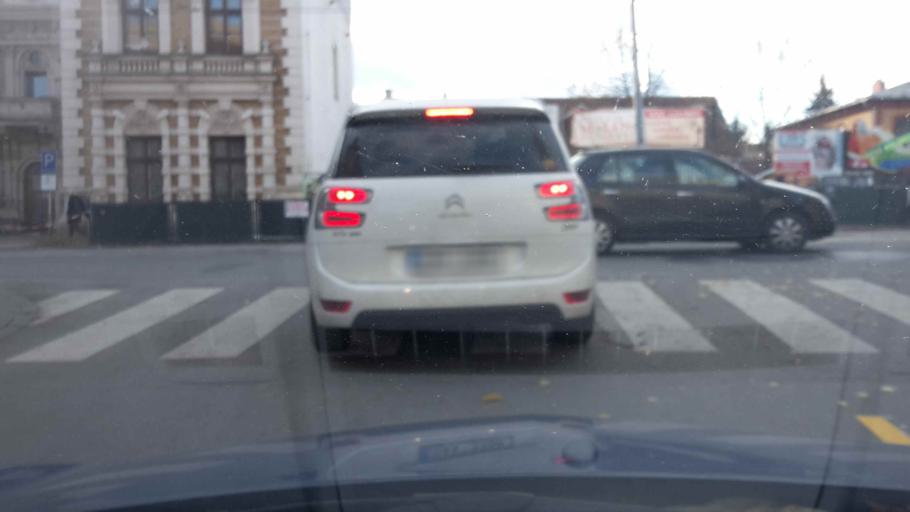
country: CZ
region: South Moravian
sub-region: Mesto Brno
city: Brno
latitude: 49.2268
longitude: 16.5934
